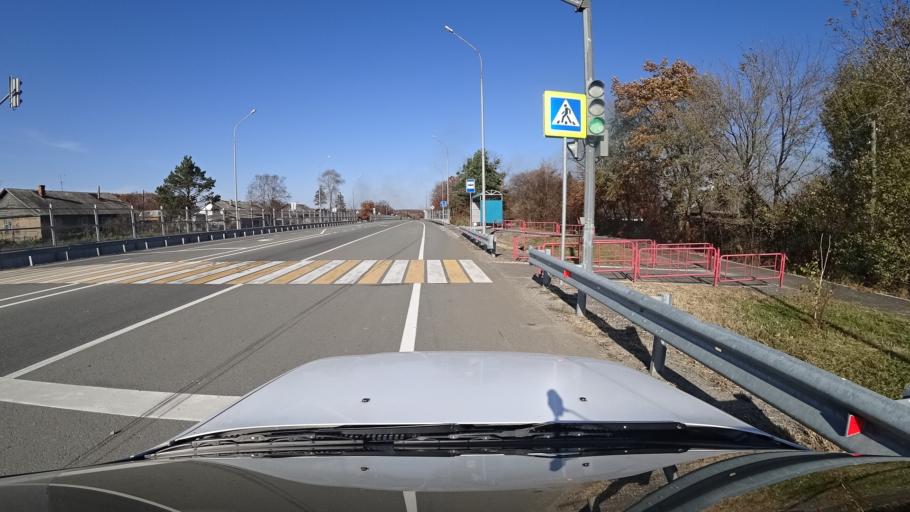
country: RU
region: Primorskiy
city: Dal'nerechensk
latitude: 45.8806
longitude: 133.7285
